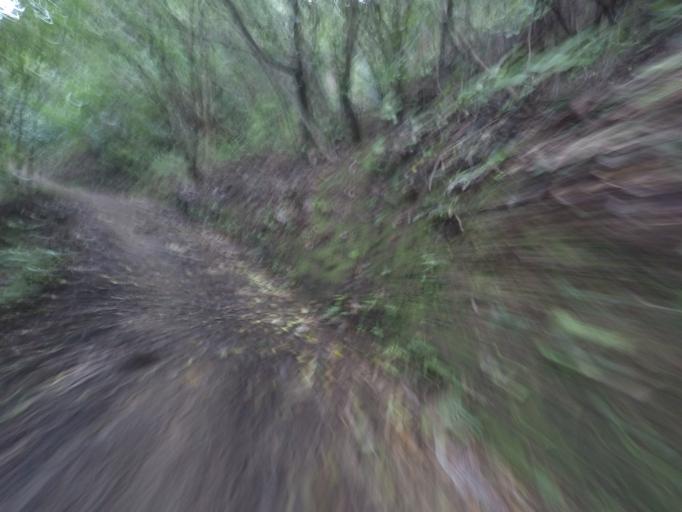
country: NZ
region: Bay of Plenty
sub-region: Western Bay of Plenty District
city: Waihi Beach
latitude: -37.3905
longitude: 175.9400
